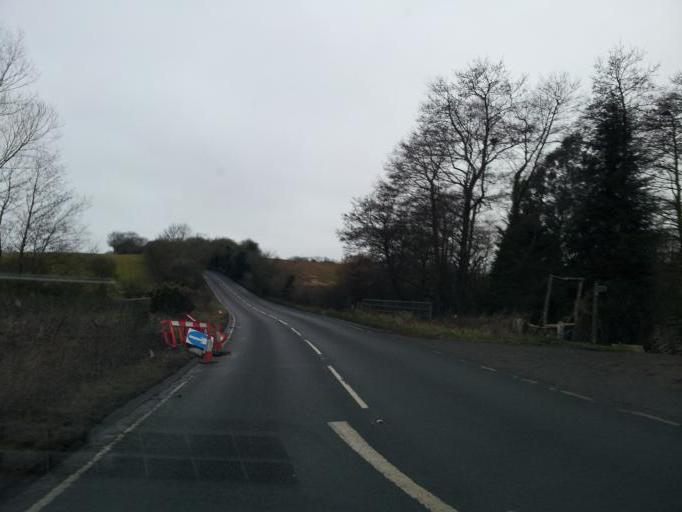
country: GB
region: England
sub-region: Essex
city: Mistley
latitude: 51.9742
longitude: 1.0909
